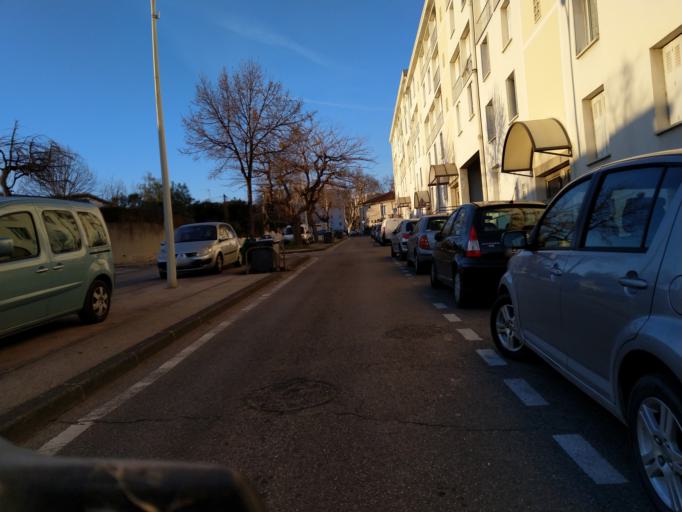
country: FR
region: Provence-Alpes-Cote d'Azur
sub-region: Departement des Bouches-du-Rhone
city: Marseille 12
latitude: 43.2964
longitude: 5.4384
